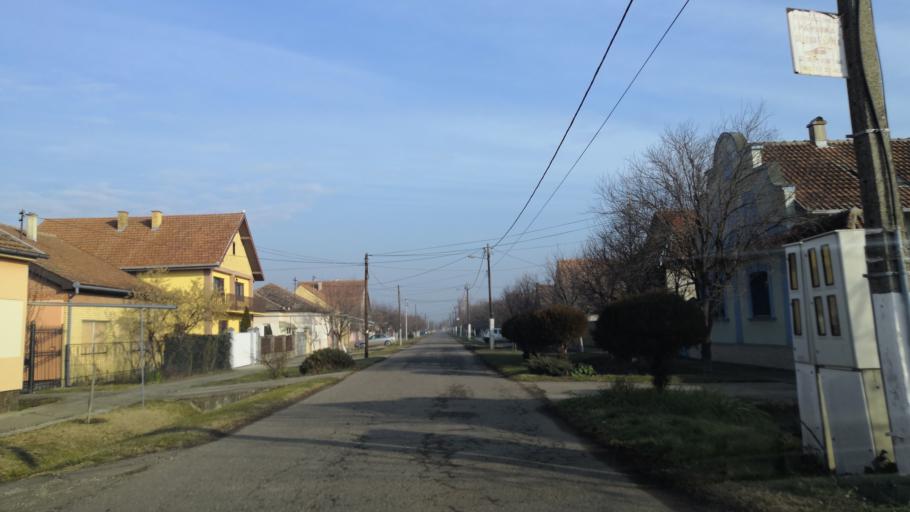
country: RS
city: Kisac
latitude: 45.3501
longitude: 19.7340
